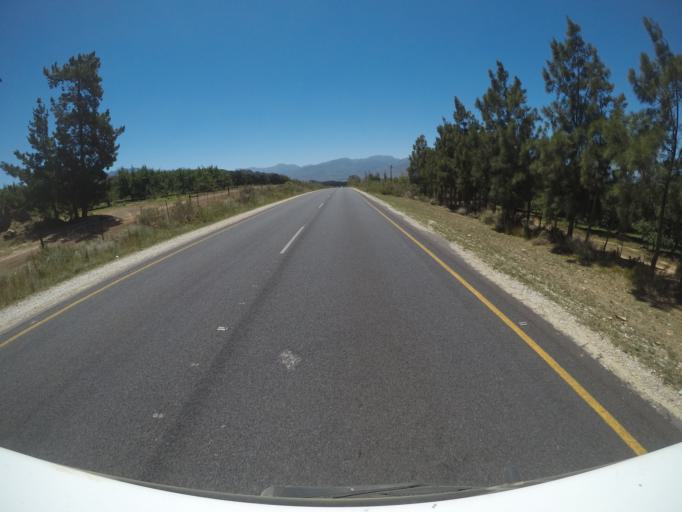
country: ZA
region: Western Cape
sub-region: Overberg District Municipality
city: Grabouw
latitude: -34.0642
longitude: 19.1339
